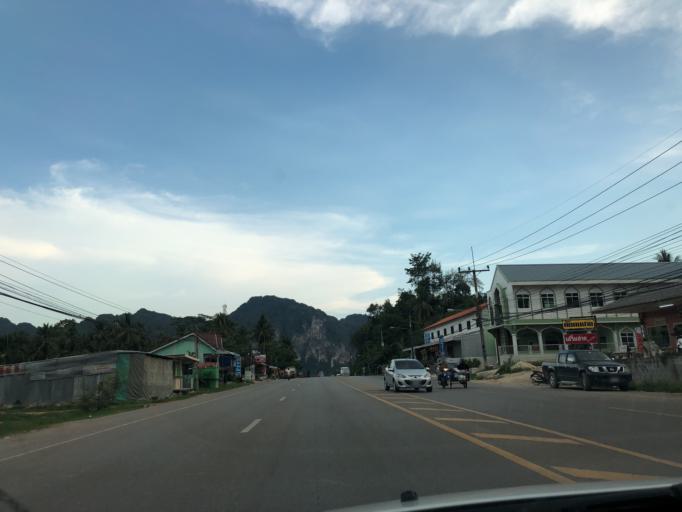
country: TH
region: Phangnga
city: Ban Ao Nang
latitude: 8.0471
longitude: 98.8377
